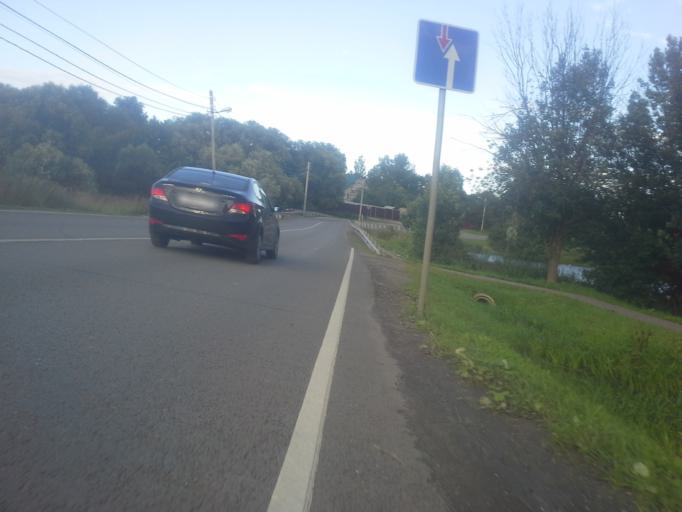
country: RU
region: Moskovskaya
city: Zhavoronki
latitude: 55.6659
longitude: 37.0826
